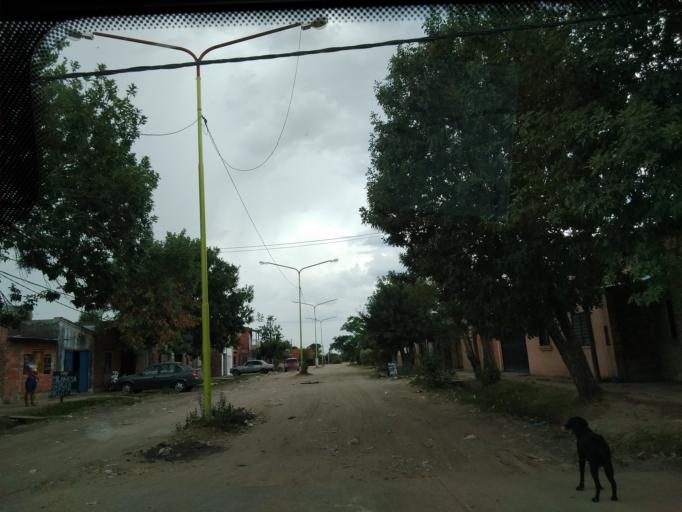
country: AR
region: Corrientes
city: Corrientes
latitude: -27.5230
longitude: -58.7887
